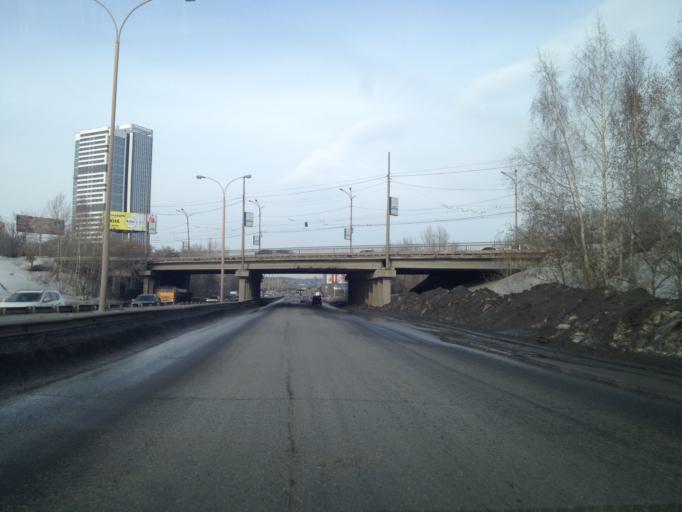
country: RU
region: Sverdlovsk
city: Yekaterinburg
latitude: 56.7943
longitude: 60.6401
